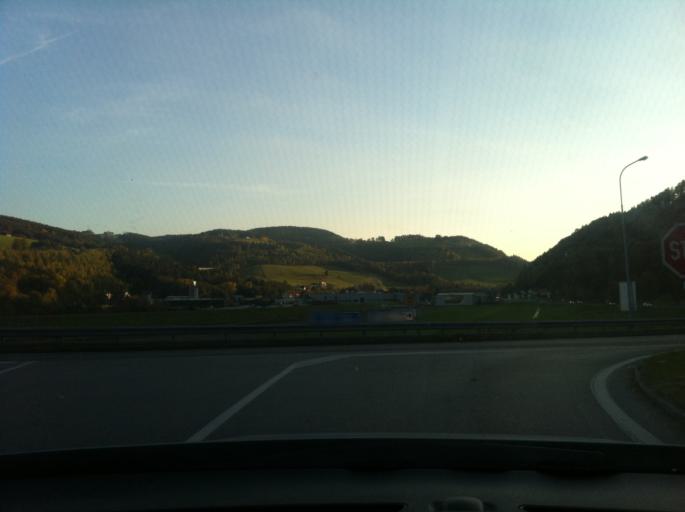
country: AT
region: Lower Austria
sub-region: Politischer Bezirk Neunkirchen
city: Grimmenstein
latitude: 47.6072
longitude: 16.1208
